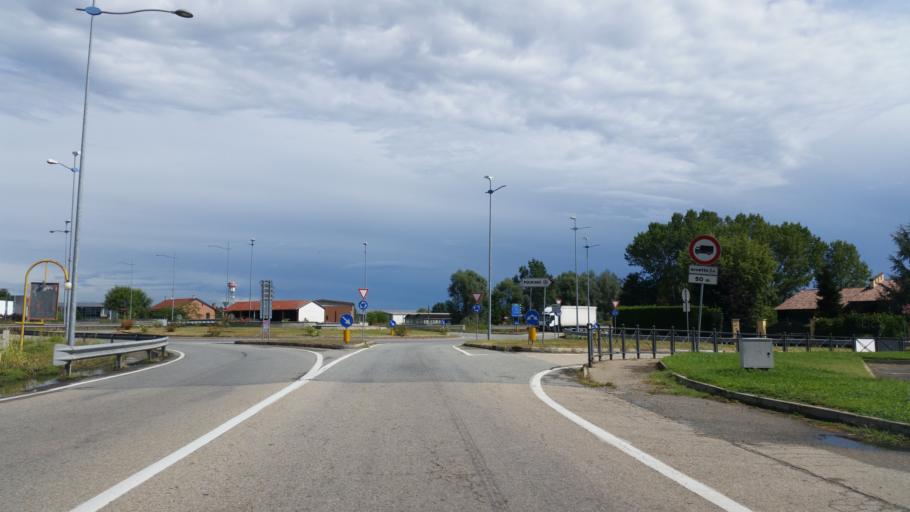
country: IT
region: Piedmont
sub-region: Provincia di Torino
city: Poirino
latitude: 44.9237
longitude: 7.8381
